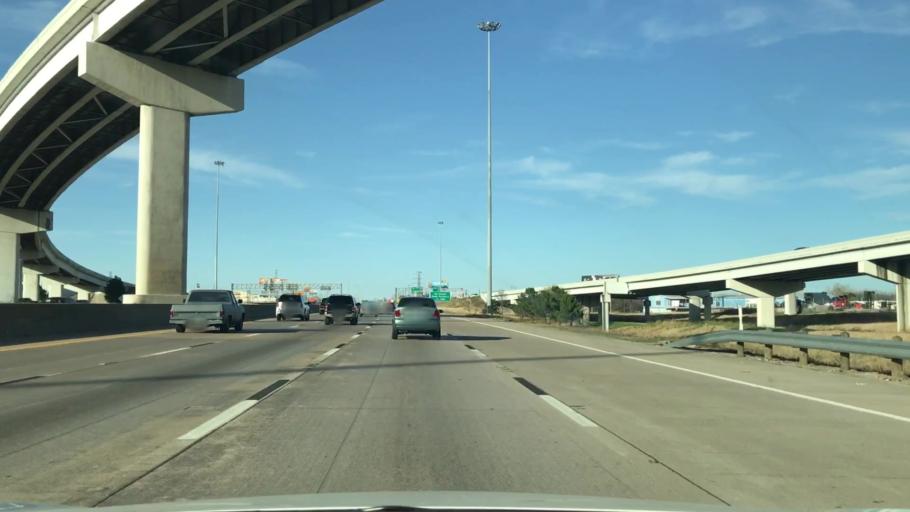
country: US
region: Texas
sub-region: Tarrant County
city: Edgecliff Village
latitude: 32.6682
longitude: -97.3205
